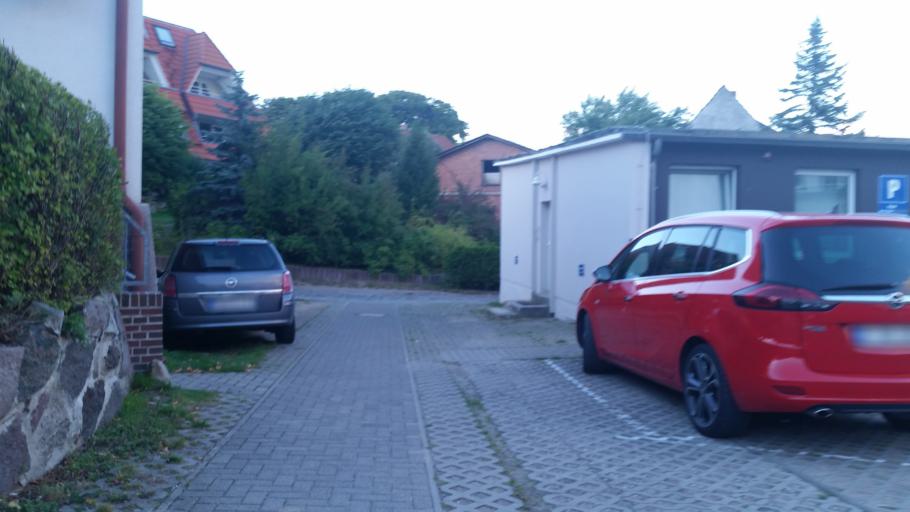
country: DE
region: Mecklenburg-Vorpommern
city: Altenkirchen
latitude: 54.6126
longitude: 13.3539
